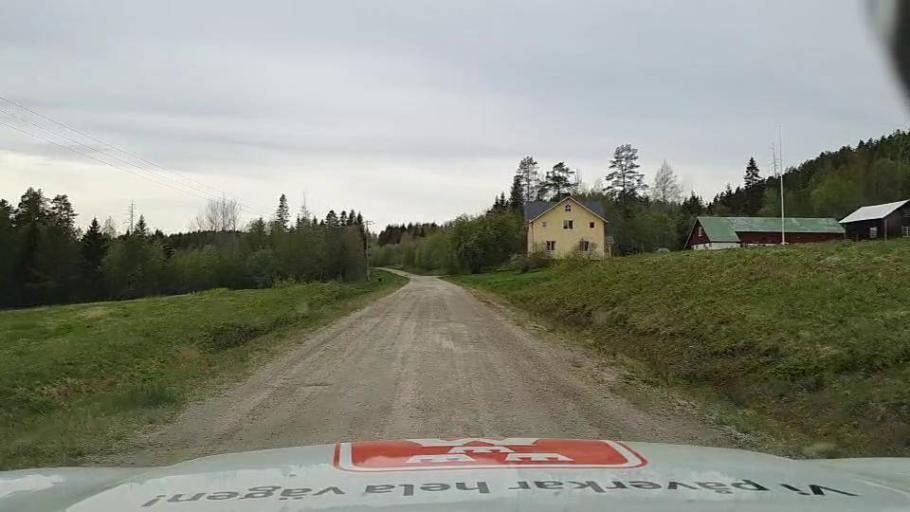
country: SE
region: Jaemtland
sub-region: Bergs Kommun
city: Hoverberg
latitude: 62.6673
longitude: 14.8173
